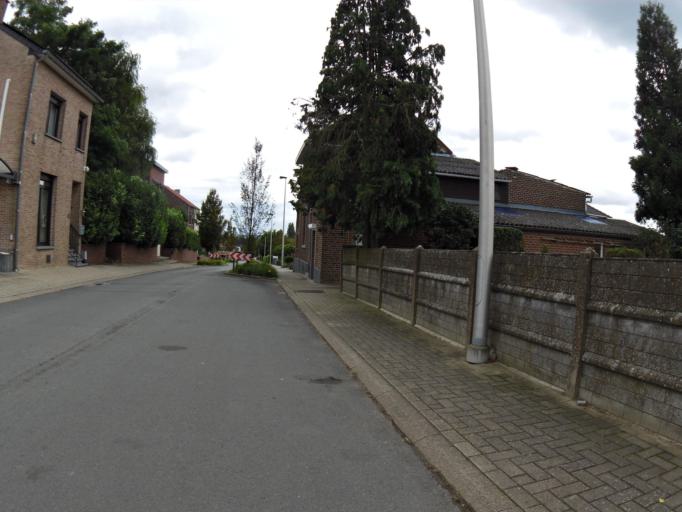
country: BE
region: Flanders
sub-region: Provincie Limburg
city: Tongeren
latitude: 50.7903
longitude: 5.4970
